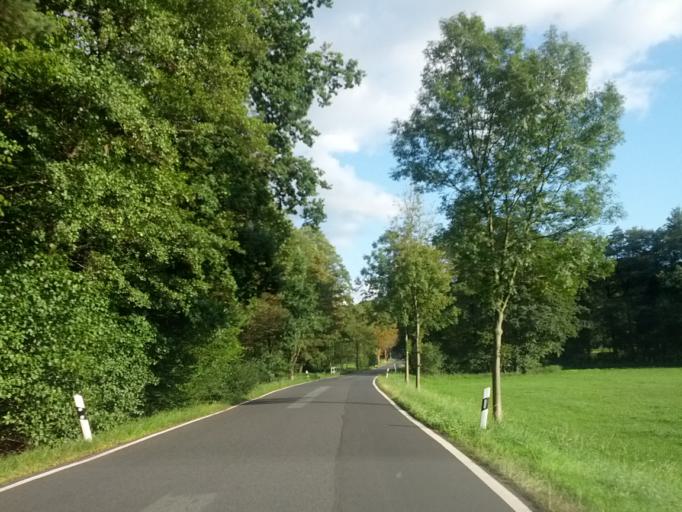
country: DE
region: Thuringia
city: Wolfsburg-Unkeroda
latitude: 50.9271
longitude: 10.2864
